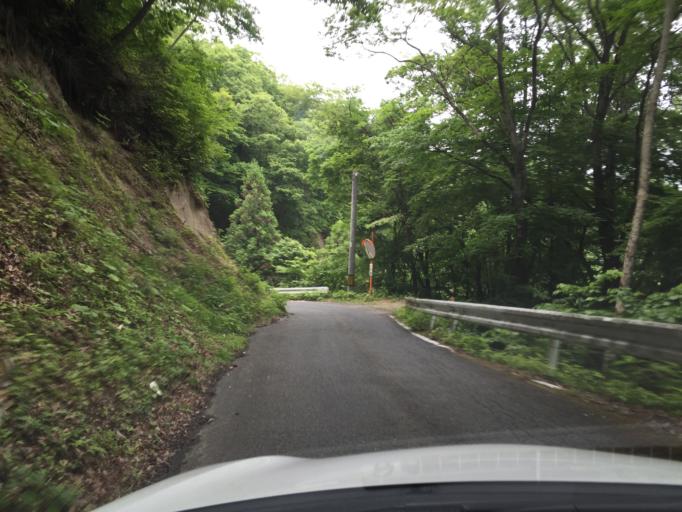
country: JP
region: Fukushima
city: Iwaki
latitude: 37.2088
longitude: 140.7227
